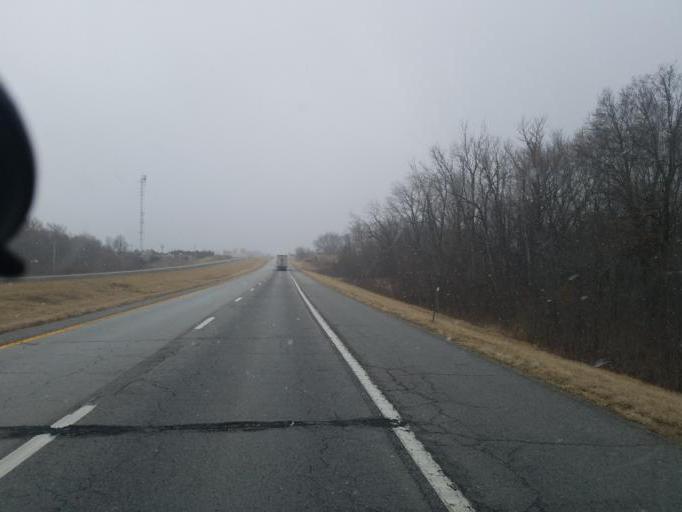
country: US
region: Missouri
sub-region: Macon County
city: La Plata
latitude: 39.9238
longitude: -92.4754
